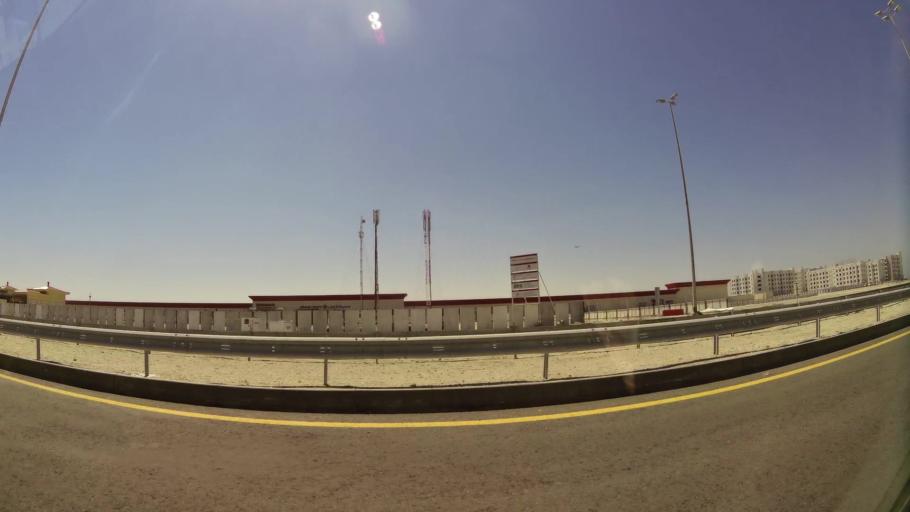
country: BH
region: Muharraq
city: Al Muharraq
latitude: 26.3082
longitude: 50.6260
